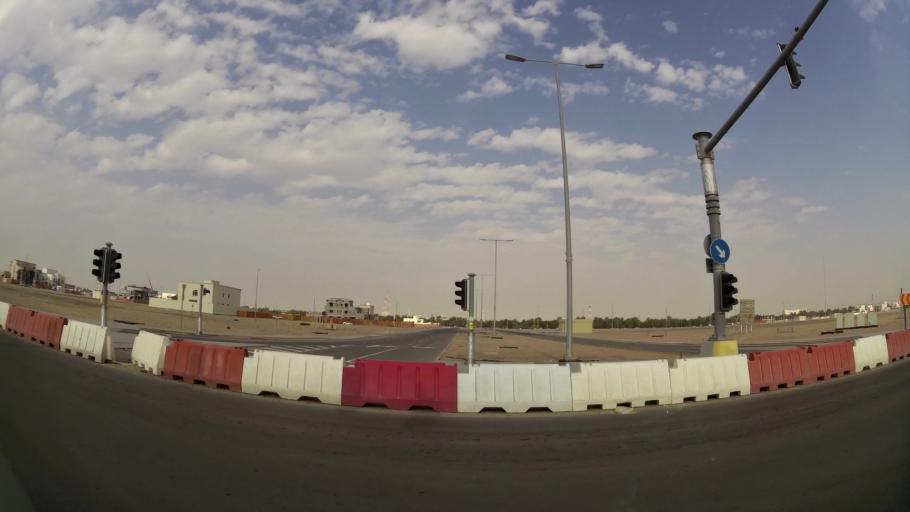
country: AE
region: Abu Dhabi
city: Abu Dhabi
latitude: 24.3363
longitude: 54.5701
